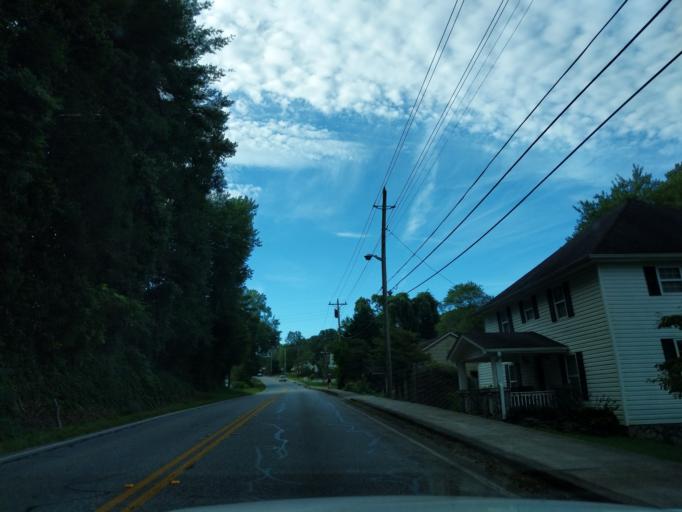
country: US
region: Georgia
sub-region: Fannin County
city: McCaysville
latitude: 34.9789
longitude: -84.3731
